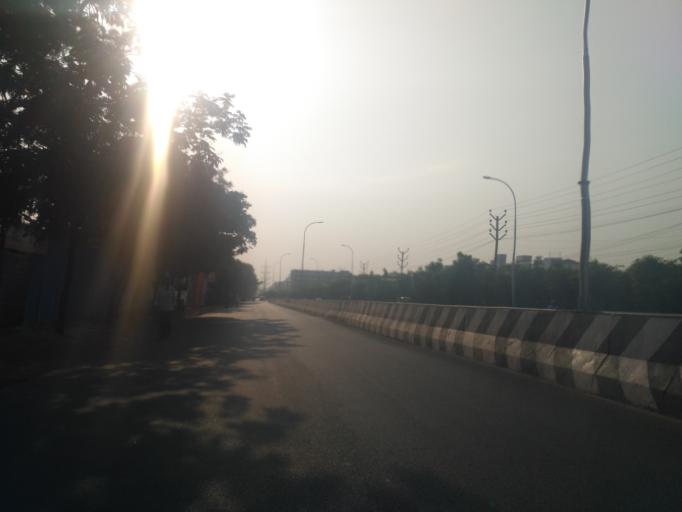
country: IN
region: Telangana
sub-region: Rangareddi
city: Kukatpalli
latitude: 17.4527
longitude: 78.3833
